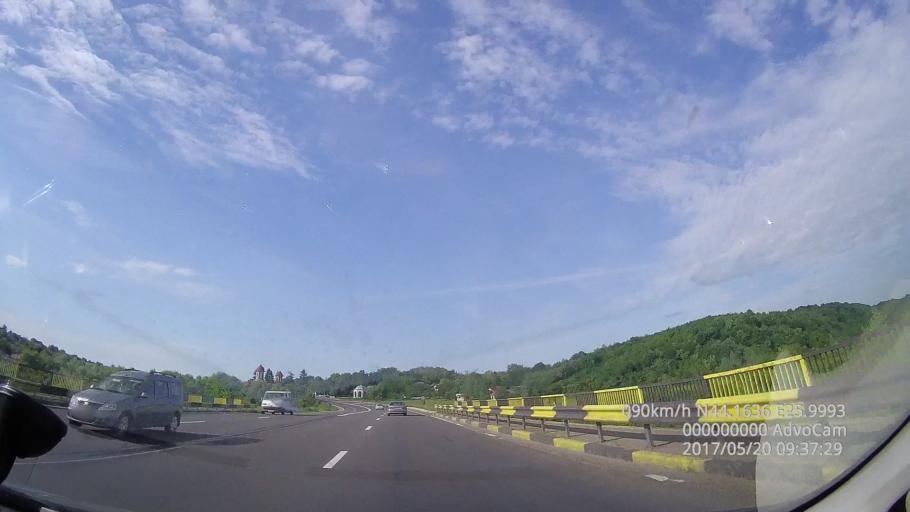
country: RO
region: Giurgiu
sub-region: Comuna Calugareni
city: Calugareni
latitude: 44.1633
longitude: 25.9991
